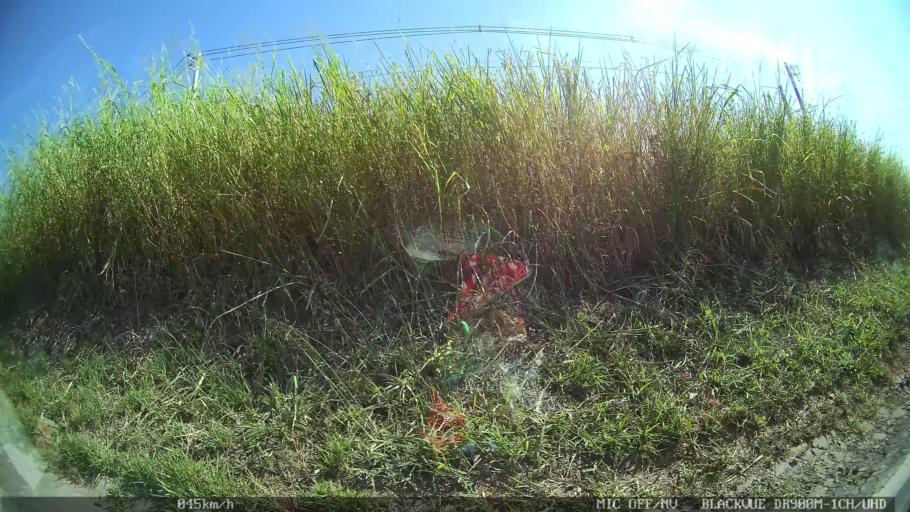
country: BR
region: Sao Paulo
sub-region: Valinhos
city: Valinhos
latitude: -23.0176
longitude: -47.0943
